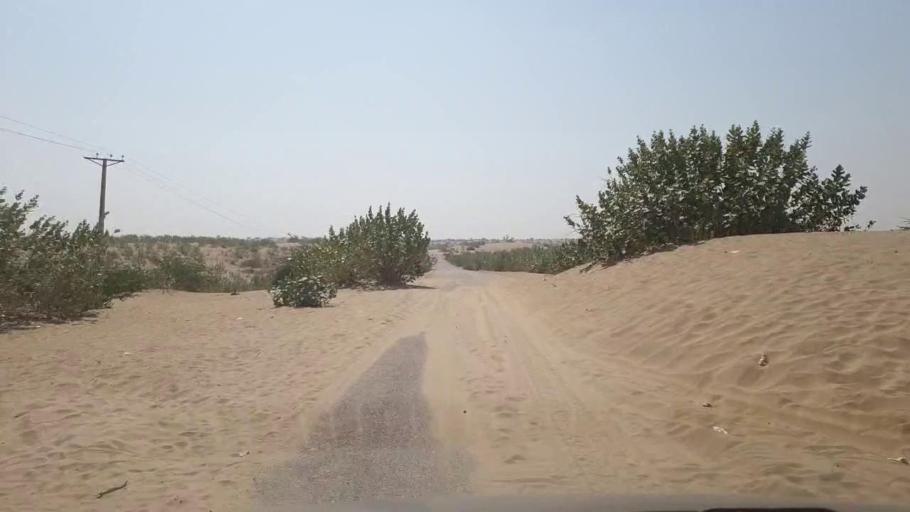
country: PK
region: Sindh
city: Chor
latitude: 25.6663
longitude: 70.1671
